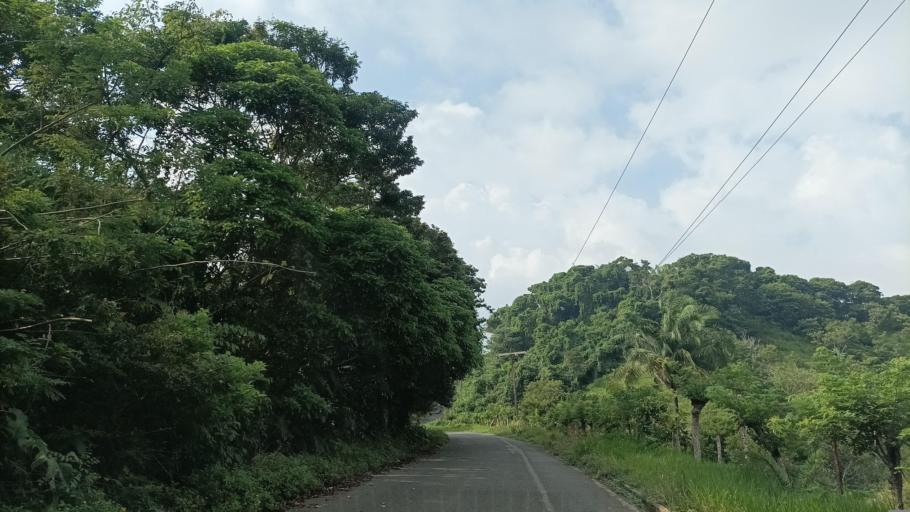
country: MX
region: Veracruz
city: Allende
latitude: 18.1287
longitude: -94.2842
